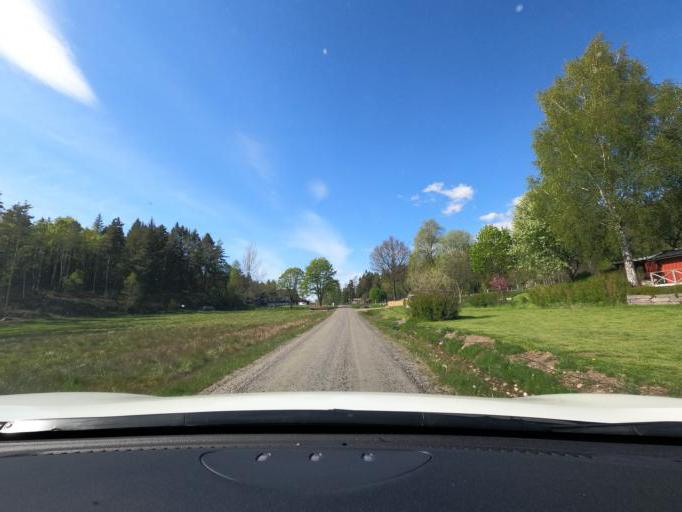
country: SE
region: Vaestra Goetaland
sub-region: Harryda Kommun
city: Ravlanda
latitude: 57.5899
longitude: 12.4883
